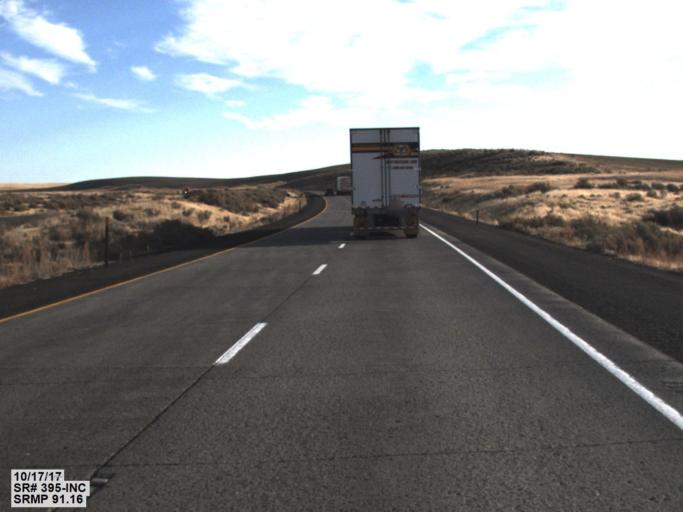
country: US
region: Washington
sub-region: Adams County
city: Ritzville
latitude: 47.0518
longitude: -118.4266
